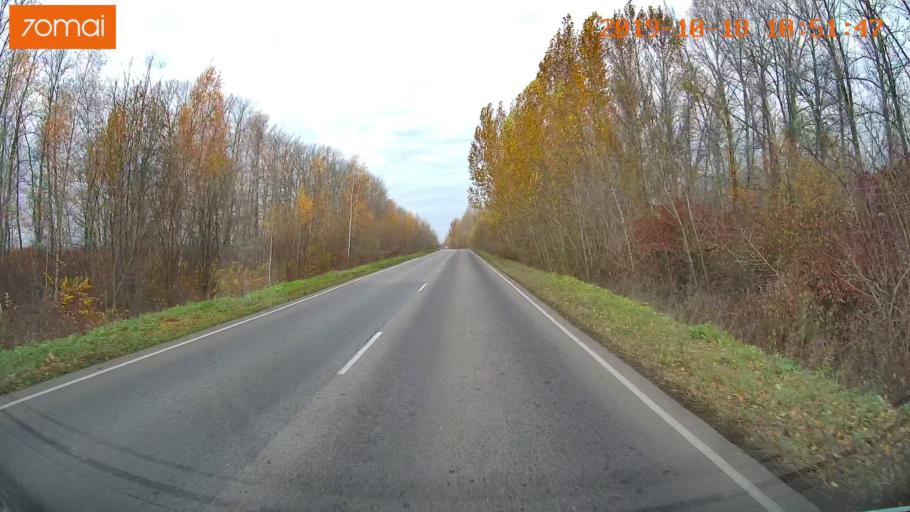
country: RU
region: Tula
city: Yepifan'
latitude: 53.7587
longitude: 38.6623
